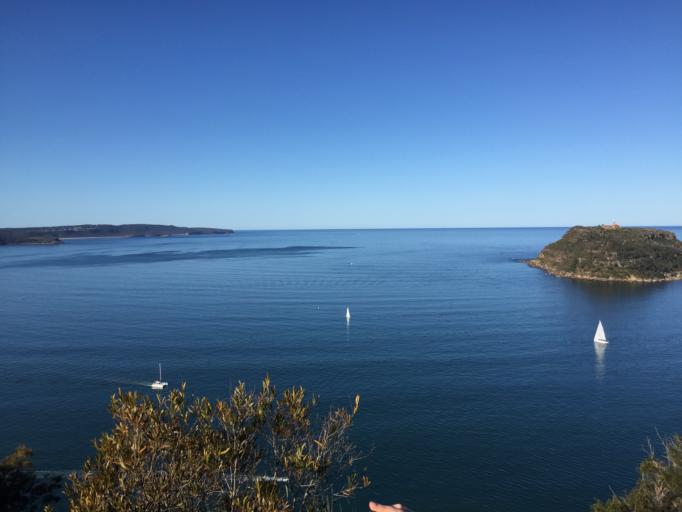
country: AU
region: New South Wales
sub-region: Pittwater
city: Palm Beach
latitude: -33.5791
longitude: 151.3093
